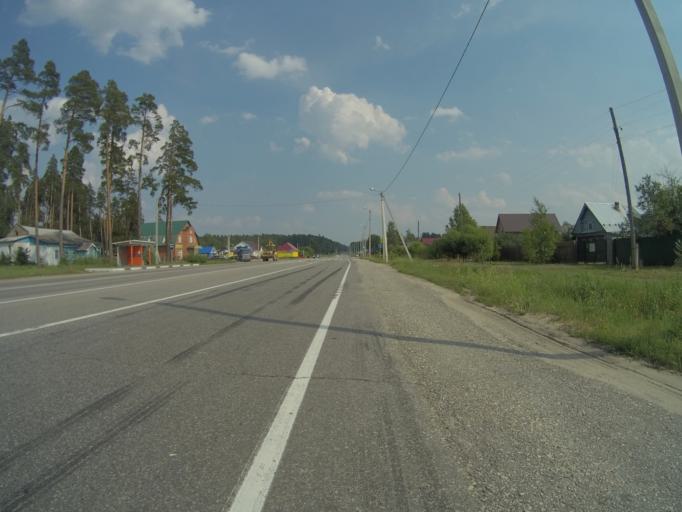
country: RU
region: Vladimir
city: Andreyevo
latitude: 55.9286
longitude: 41.1173
